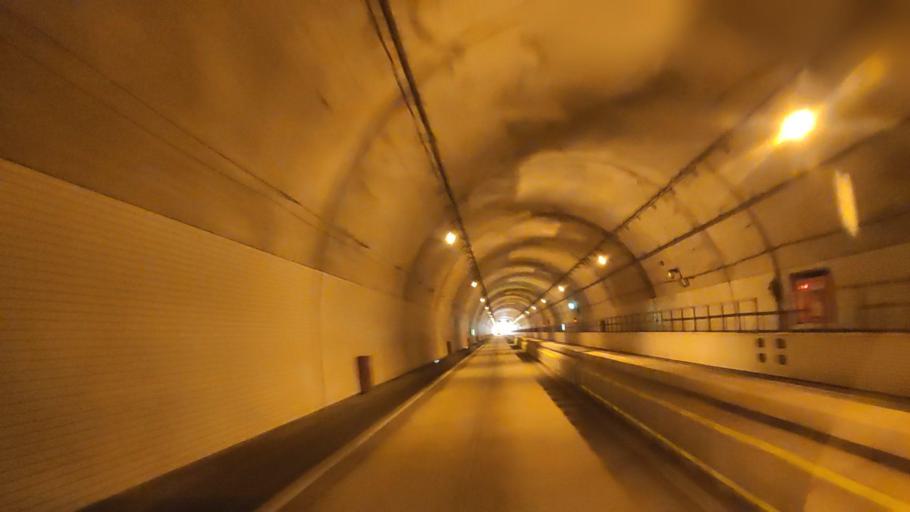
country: JP
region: Toyama
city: Nyuzen
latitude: 36.9630
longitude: 137.5882
